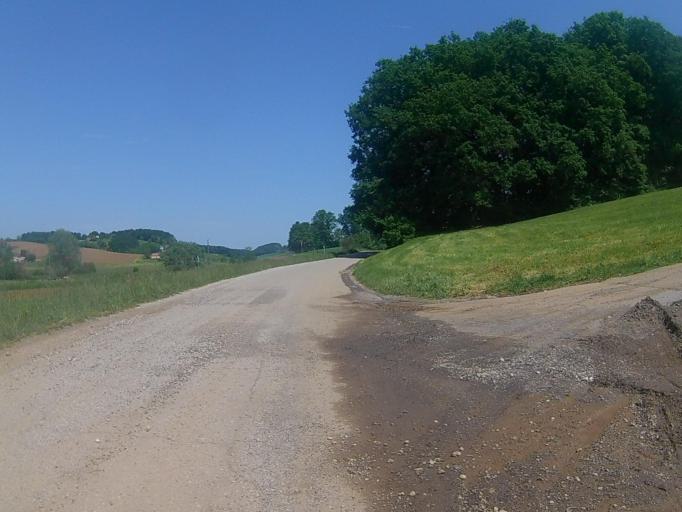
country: SI
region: Sveti Jurij v Slovenskih Goricah
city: Jurovski Dol
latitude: 46.5971
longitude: 15.7435
